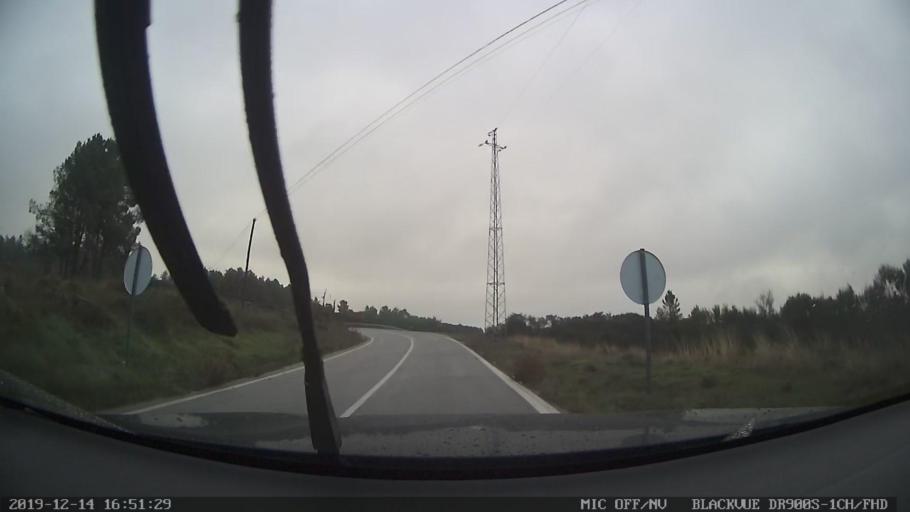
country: PT
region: Vila Real
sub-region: Murca
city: Murca
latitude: 41.4236
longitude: -7.5045
